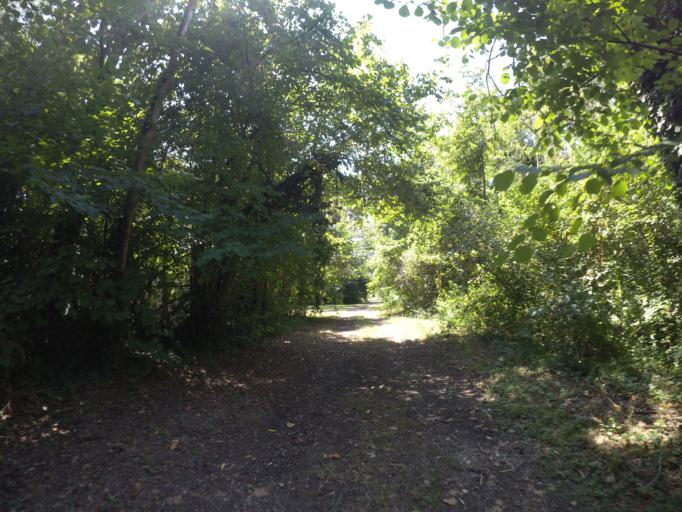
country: IT
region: Friuli Venezia Giulia
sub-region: Provincia di Udine
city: Rivignano
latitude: 45.8972
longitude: 13.0661
